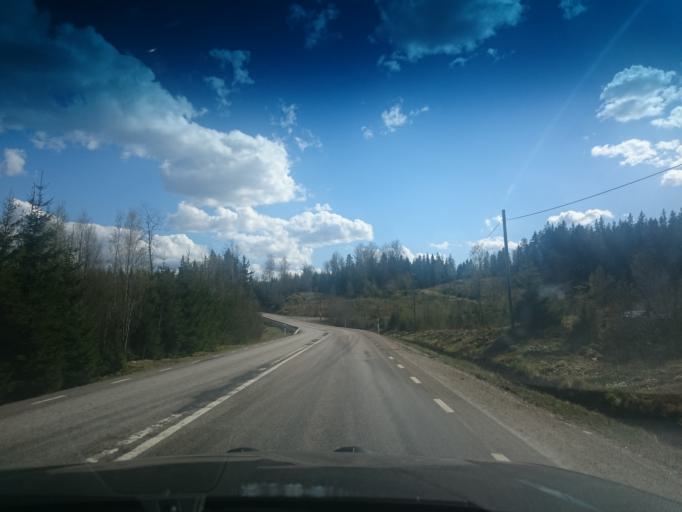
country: SE
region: Joenkoeping
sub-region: Vetlanda Kommun
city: Vetlanda
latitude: 57.2718
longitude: 15.1272
